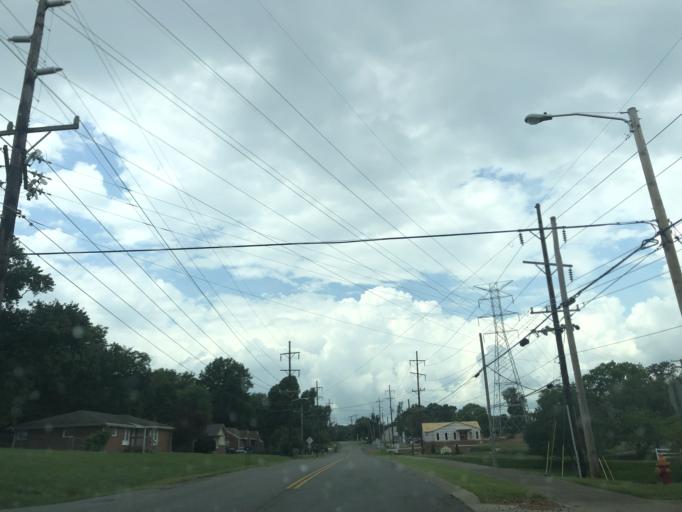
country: US
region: Tennessee
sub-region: Davidson County
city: Lakewood
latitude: 36.1615
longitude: -86.6590
